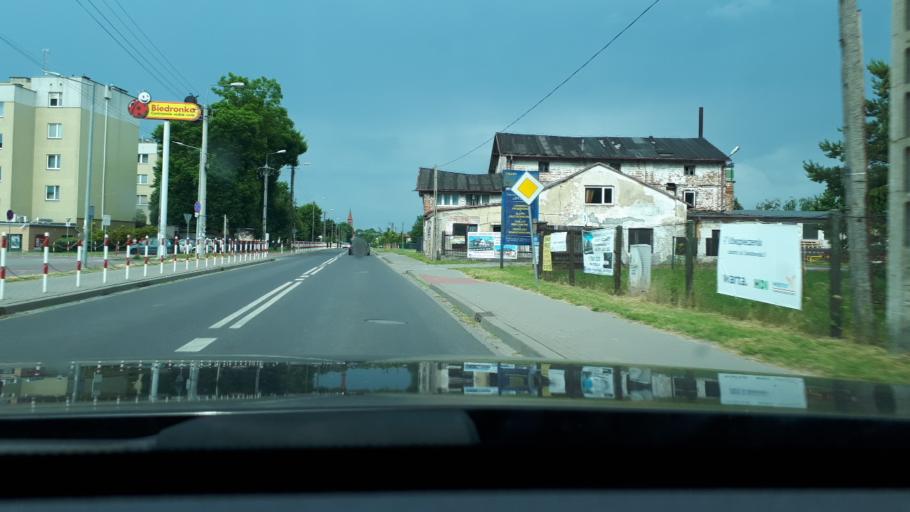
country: PL
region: Masovian Voivodeship
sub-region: Powiat warszawski zachodni
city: Leszno
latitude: 52.2575
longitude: 20.5787
